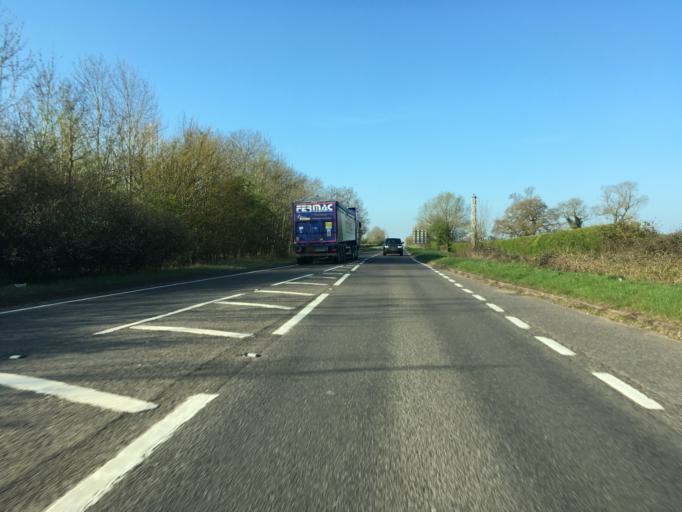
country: GB
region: England
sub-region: Northamptonshire
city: Deanshanger
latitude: 52.0417
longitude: -0.8876
